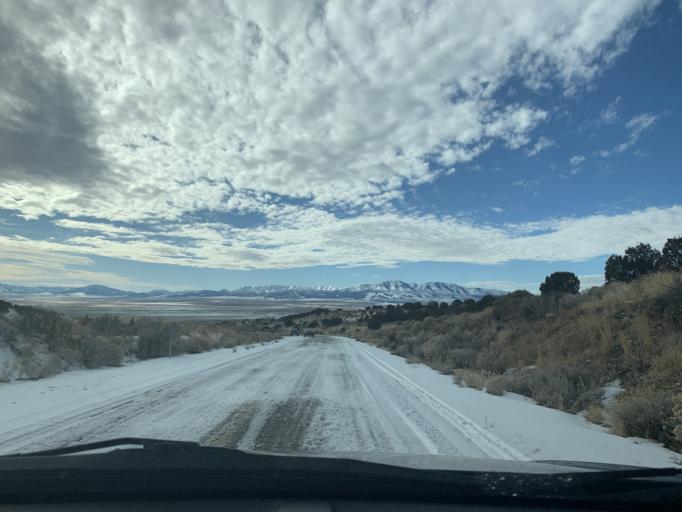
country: US
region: Utah
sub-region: Tooele County
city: Tooele
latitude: 40.3066
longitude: -112.2582
